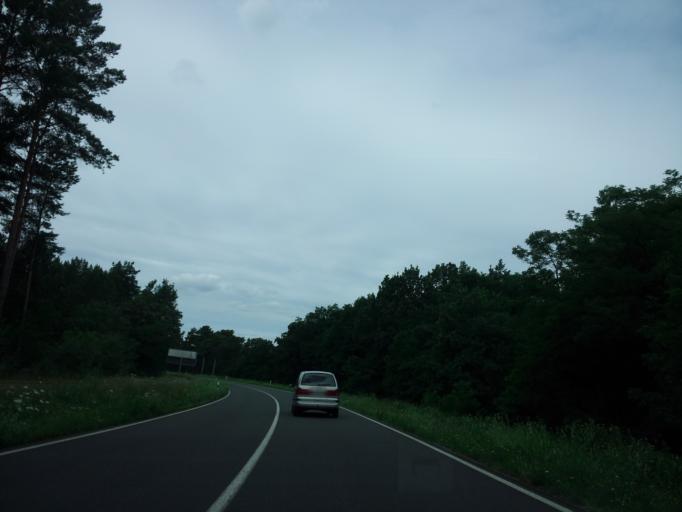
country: DE
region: Brandenburg
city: Michendorf
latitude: 52.2160
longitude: 13.0864
